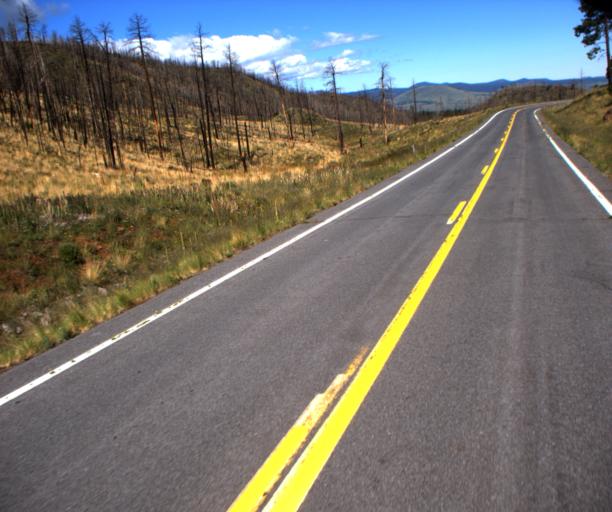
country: US
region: Arizona
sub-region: Apache County
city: Eagar
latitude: 34.0472
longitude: -109.3599
